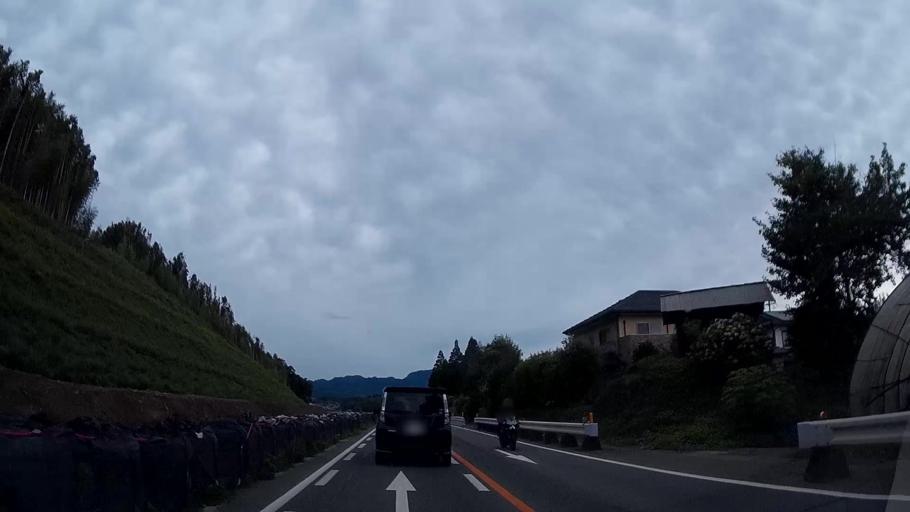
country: JP
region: Kumamoto
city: Kikuchi
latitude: 32.9555
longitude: 130.8220
